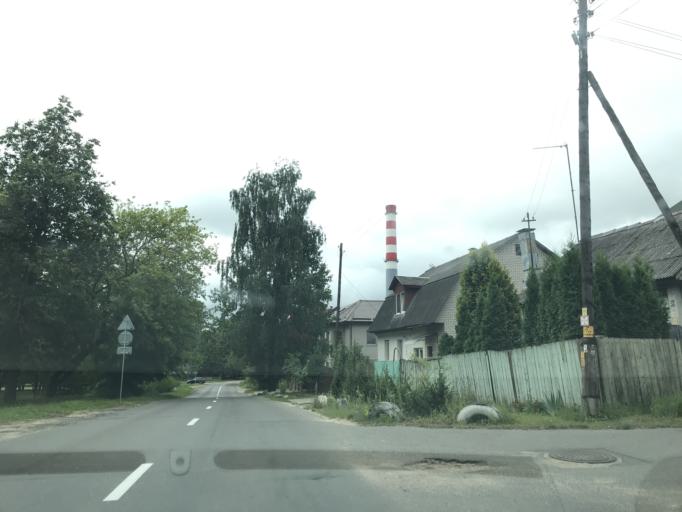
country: BY
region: Minsk
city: Minsk
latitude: 53.9360
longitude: 27.6262
